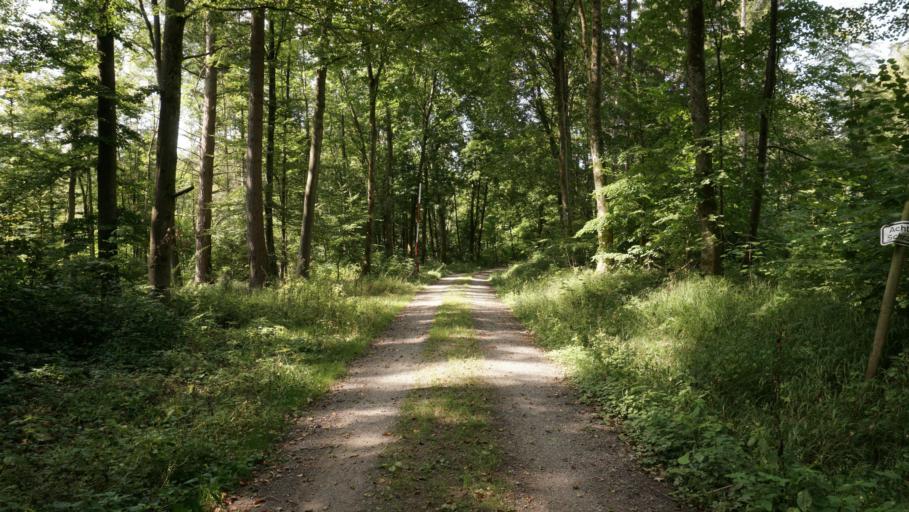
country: DE
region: Baden-Wuerttemberg
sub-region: Karlsruhe Region
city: Reichartshausen
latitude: 49.4050
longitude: 8.9554
